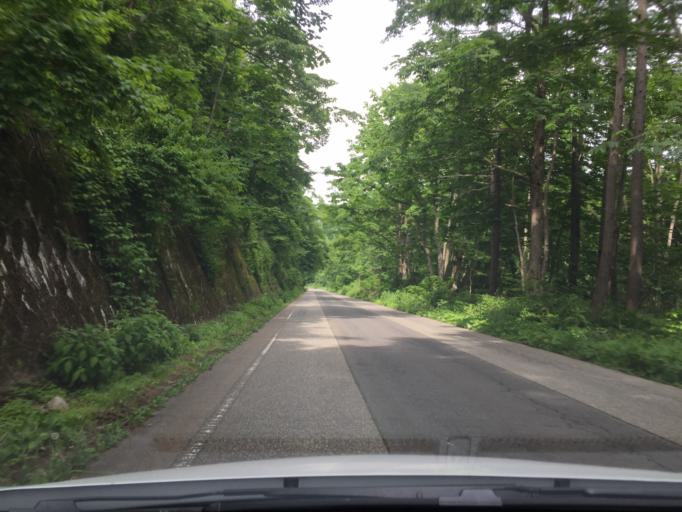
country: JP
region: Fukushima
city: Inawashiro
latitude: 37.6436
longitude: 140.0325
